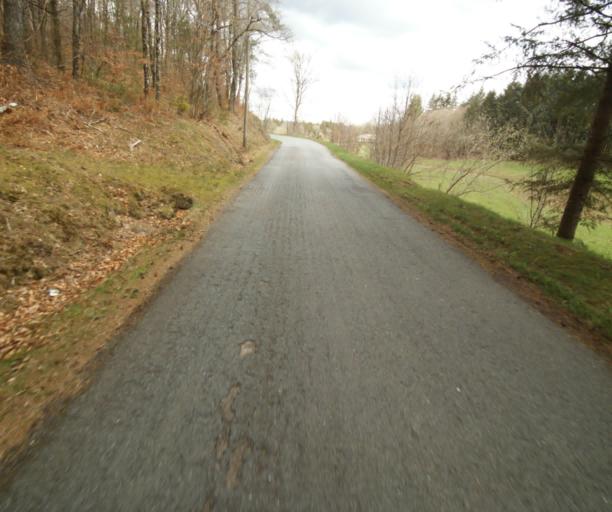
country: FR
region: Limousin
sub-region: Departement de la Correze
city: Correze
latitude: 45.3254
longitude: 1.9545
